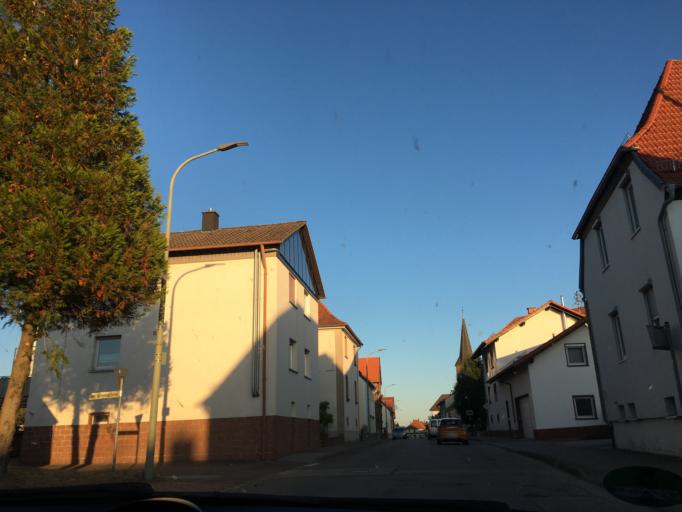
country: DE
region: Rheinland-Pfalz
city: Hermersberg
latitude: 49.3237
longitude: 7.6252
